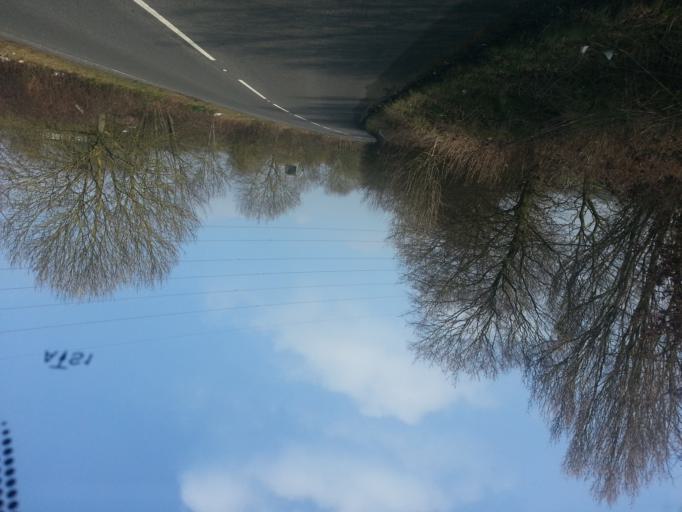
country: GB
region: England
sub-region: Greater London
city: High Barnet
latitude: 51.6837
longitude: -0.2223
